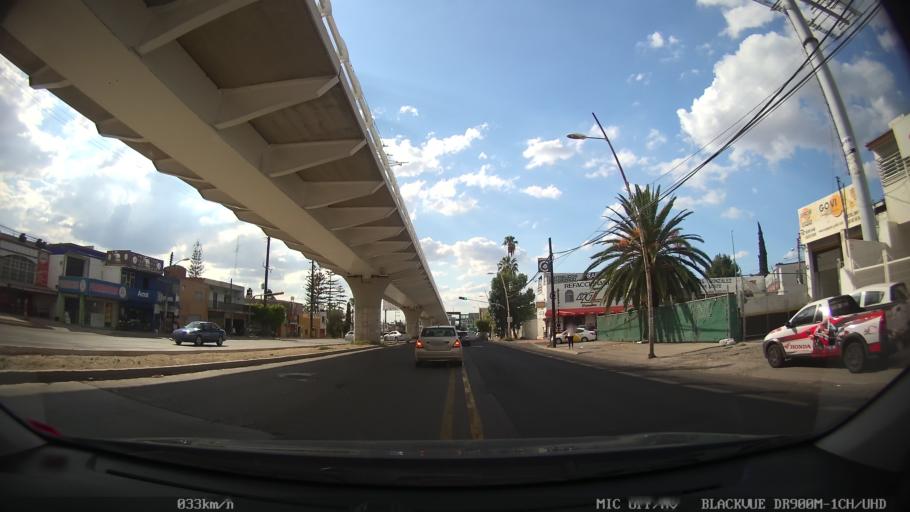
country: MX
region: Jalisco
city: Tlaquepaque
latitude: 20.6344
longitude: -103.2978
